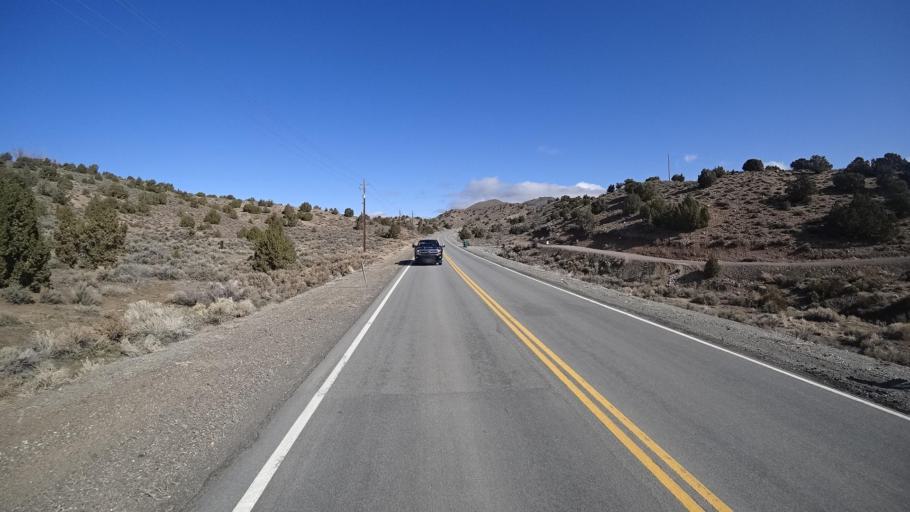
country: US
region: Nevada
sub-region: Washoe County
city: Lemmon Valley
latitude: 39.7284
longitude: -119.8812
